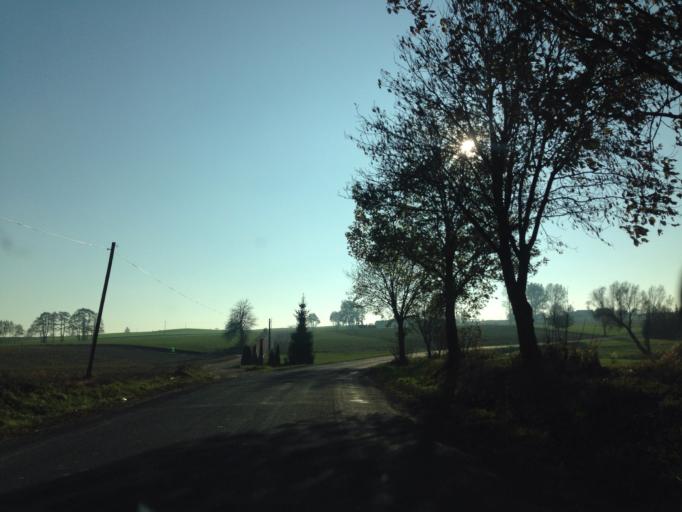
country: PL
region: Kujawsko-Pomorskie
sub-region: Powiat brodnicki
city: Swiedziebnia
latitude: 53.1638
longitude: 19.5863
